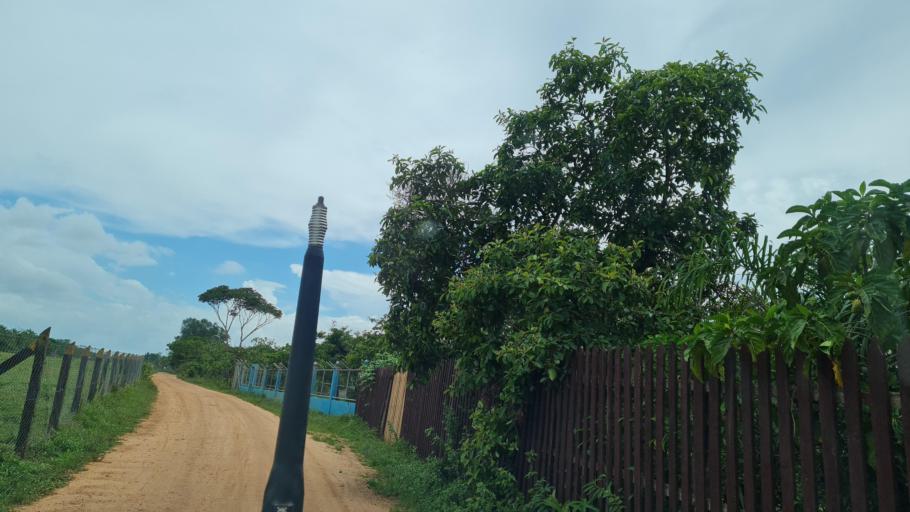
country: NI
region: Atlantico Norte (RAAN)
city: Waspam
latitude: 14.7449
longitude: -83.9655
